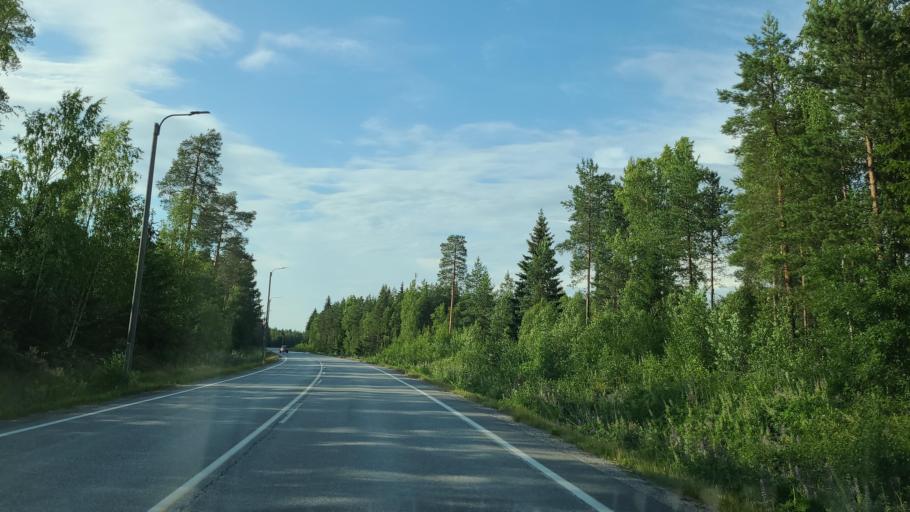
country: FI
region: Ostrobothnia
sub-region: Vaasa
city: Vaasa
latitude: 63.1383
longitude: 21.6118
